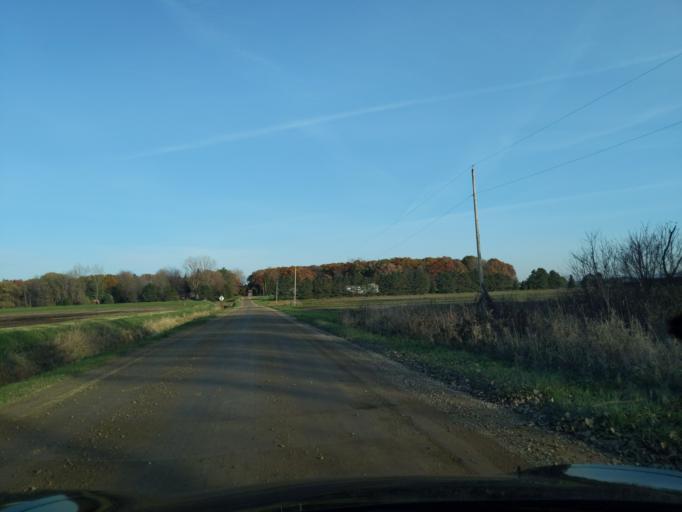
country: US
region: Michigan
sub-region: Clinton County
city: Bath
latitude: 42.7985
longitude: -84.5088
